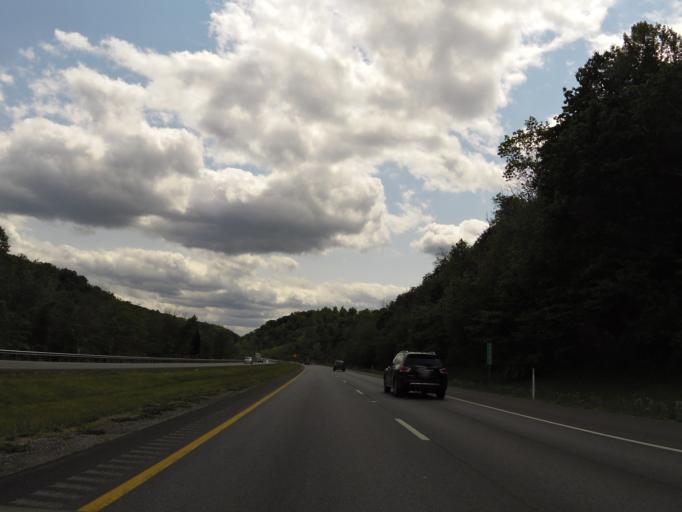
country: US
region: West Virginia
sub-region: Kanawha County
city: Sissonville
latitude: 38.5927
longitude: -81.6415
